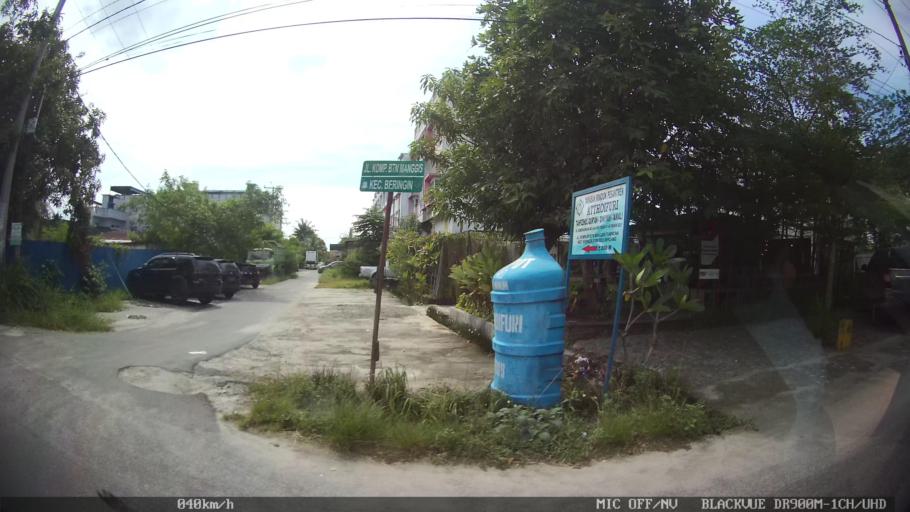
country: ID
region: North Sumatra
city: Percut
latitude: 3.5923
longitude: 98.8585
